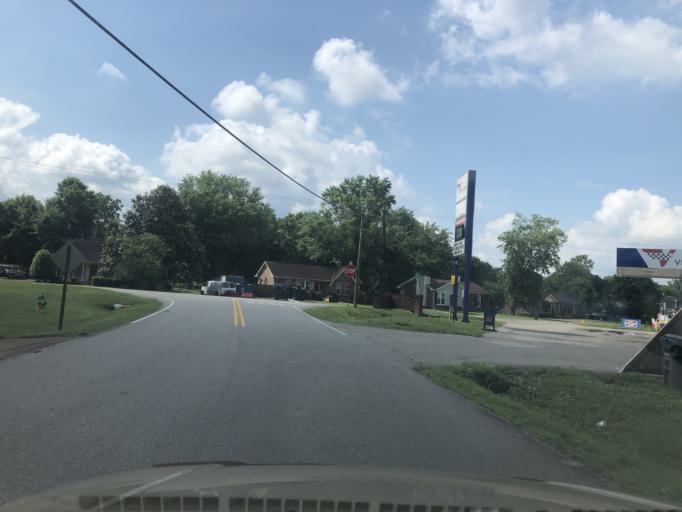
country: US
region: Tennessee
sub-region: Wilson County
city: Green Hill
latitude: 36.2309
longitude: -86.5884
